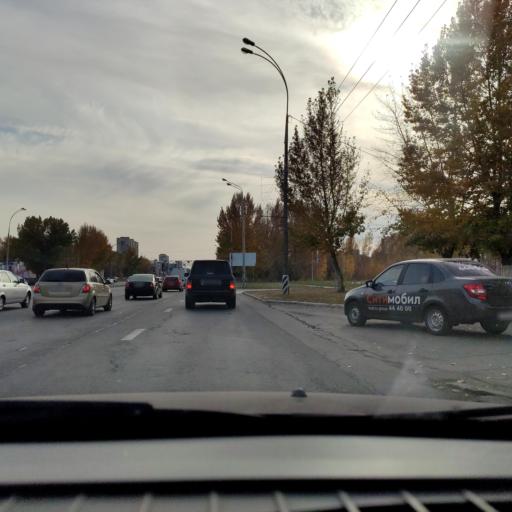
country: RU
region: Samara
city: Tol'yatti
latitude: 53.5403
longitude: 49.2842
